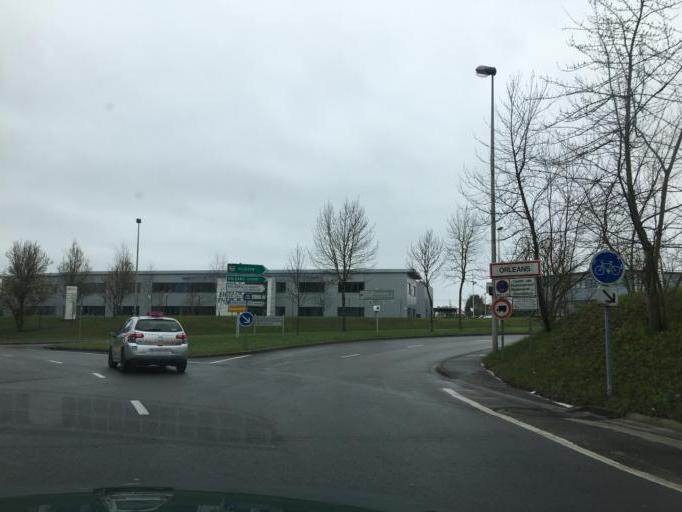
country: FR
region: Centre
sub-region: Departement du Loiret
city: Semoy
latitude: 47.9244
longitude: 1.9398
